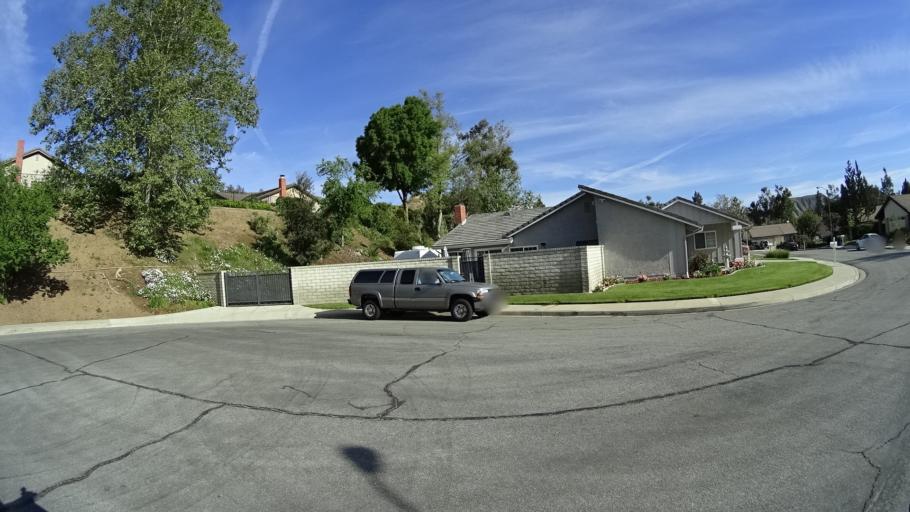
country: US
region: California
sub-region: Ventura County
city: Casa Conejo
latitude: 34.1775
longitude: -118.9582
